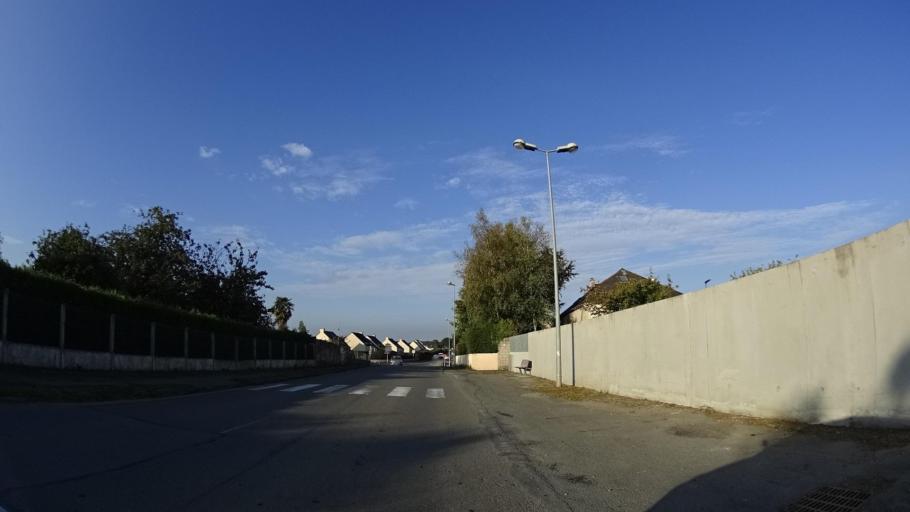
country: FR
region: Brittany
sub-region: Departement d'Ille-et-Vilaine
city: Saint-Meen-le-Grand
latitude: 48.1932
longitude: -2.1942
